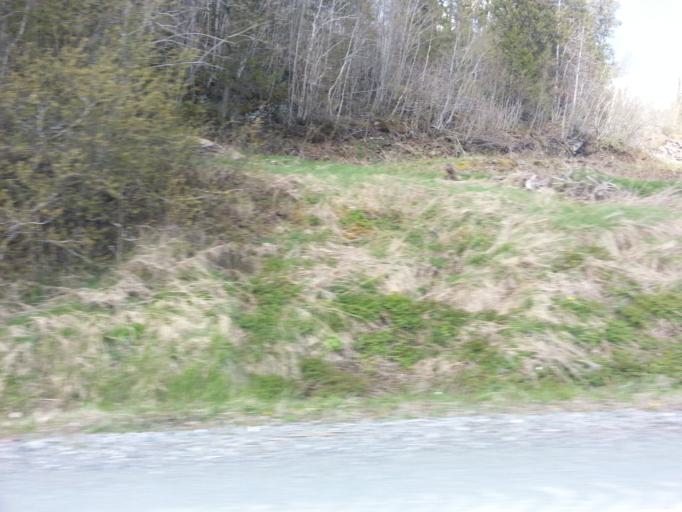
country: NO
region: Nord-Trondelag
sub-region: Levanger
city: Skogn
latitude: 63.6370
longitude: 11.2347
